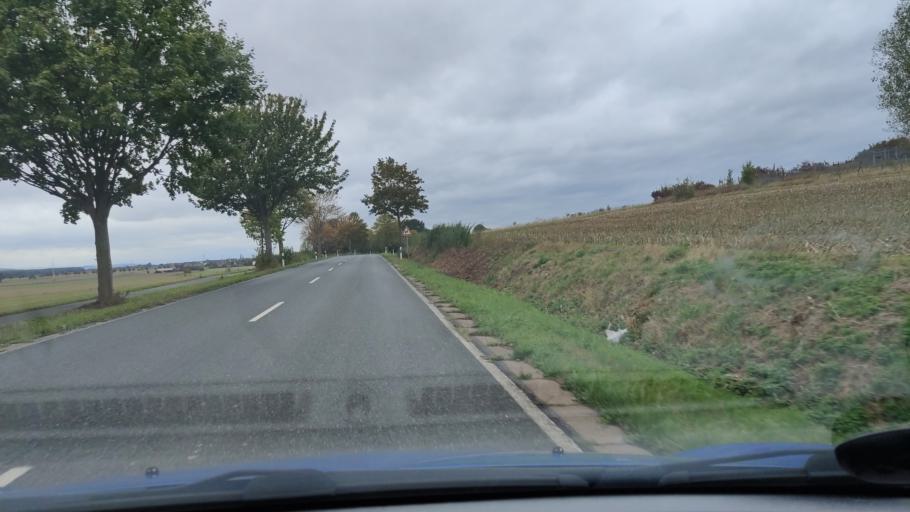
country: DE
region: Lower Saxony
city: Seelze
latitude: 52.3775
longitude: 9.6461
